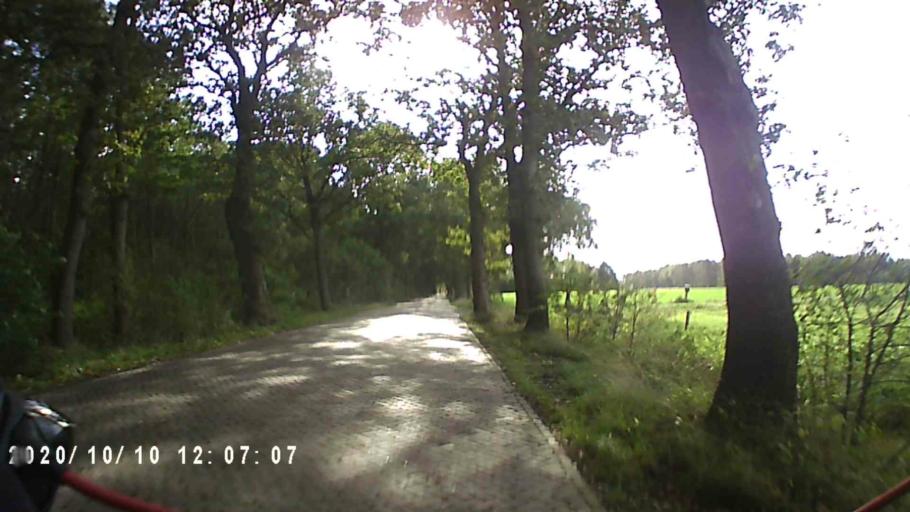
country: NL
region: Friesland
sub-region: Gemeente Heerenveen
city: Jubbega
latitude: 53.0532
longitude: 6.1380
